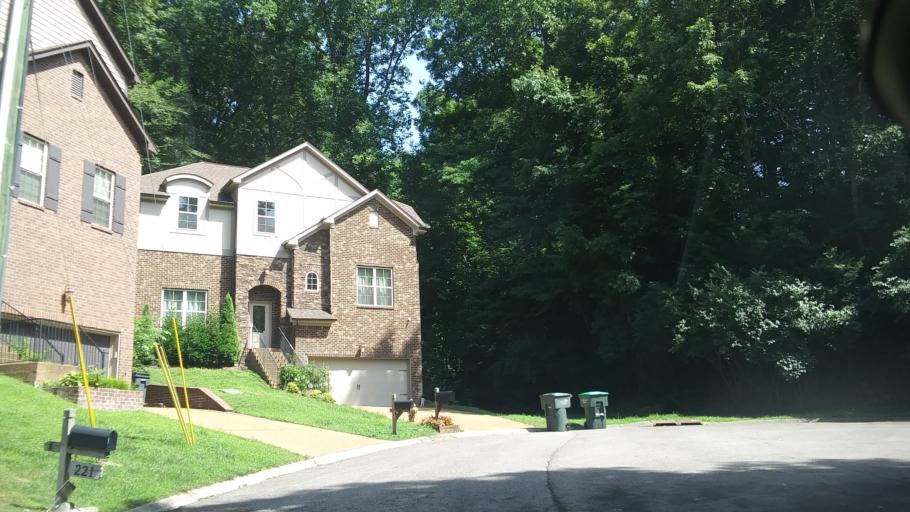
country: US
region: Tennessee
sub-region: Davidson County
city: Belle Meade
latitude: 36.0817
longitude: -86.9252
